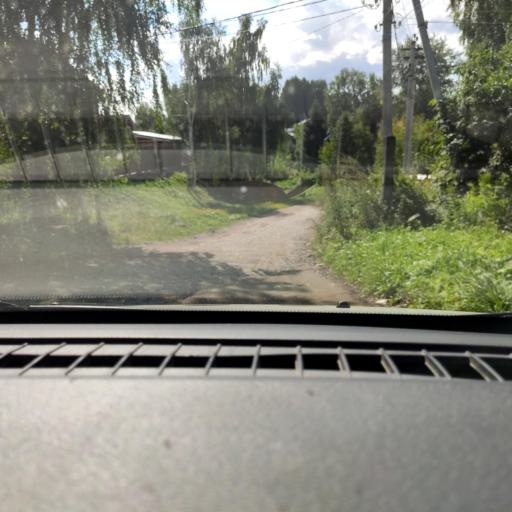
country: RU
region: Perm
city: Perm
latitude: 58.1158
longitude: 56.3932
